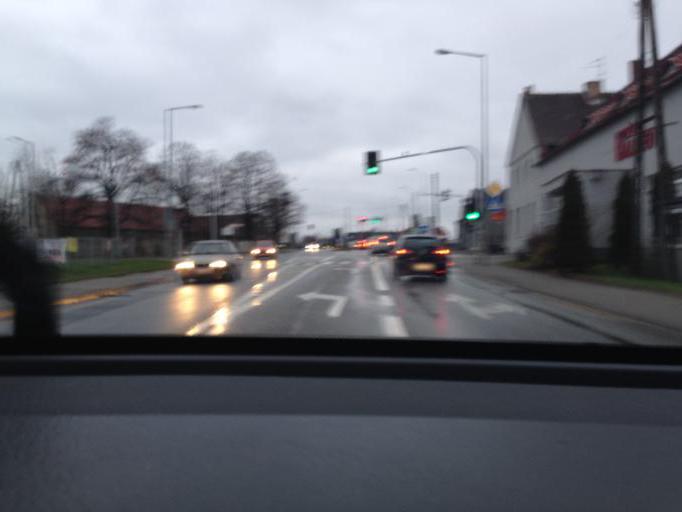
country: PL
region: Opole Voivodeship
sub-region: Powiat opolski
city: Opole
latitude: 50.6909
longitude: 17.9506
